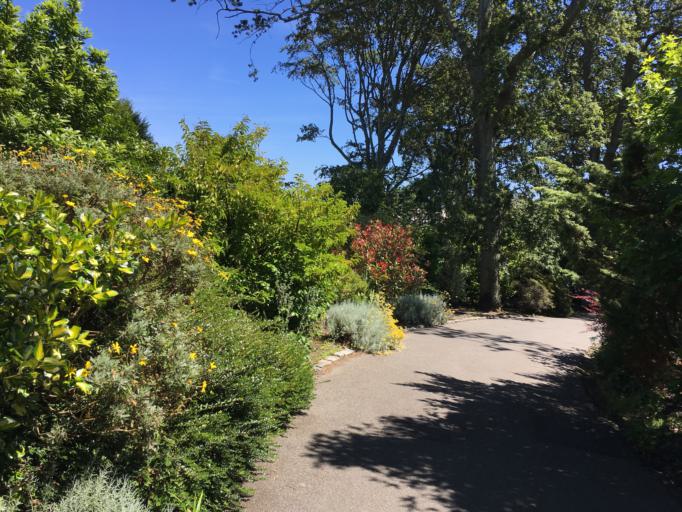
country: GG
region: St Peter Port
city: Saint Peter Port
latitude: 49.4584
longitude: -2.5397
